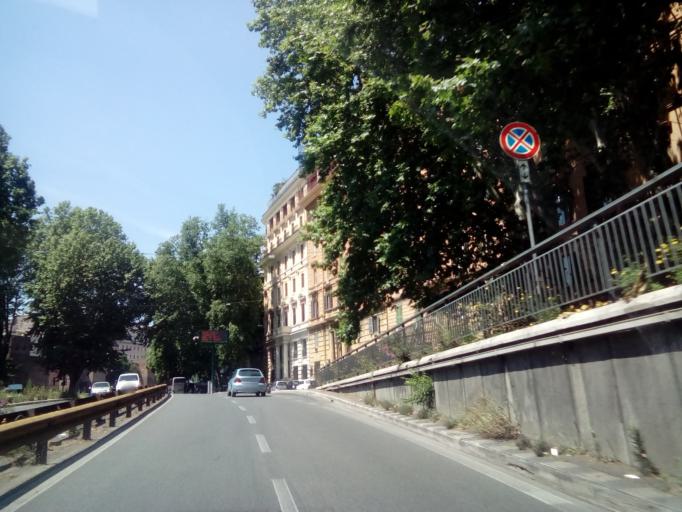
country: IT
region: Latium
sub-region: Citta metropolitana di Roma Capitale
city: Rome
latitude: 41.9107
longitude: 12.4920
